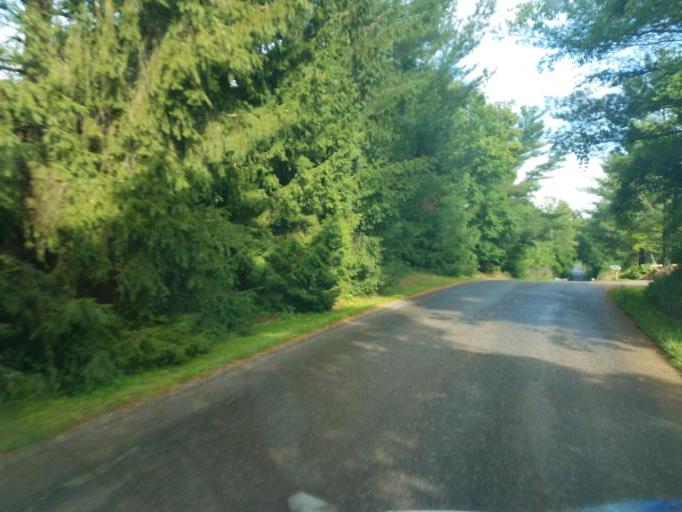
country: US
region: Ohio
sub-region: Gallia County
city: Gallipolis
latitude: 38.7694
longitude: -82.3696
